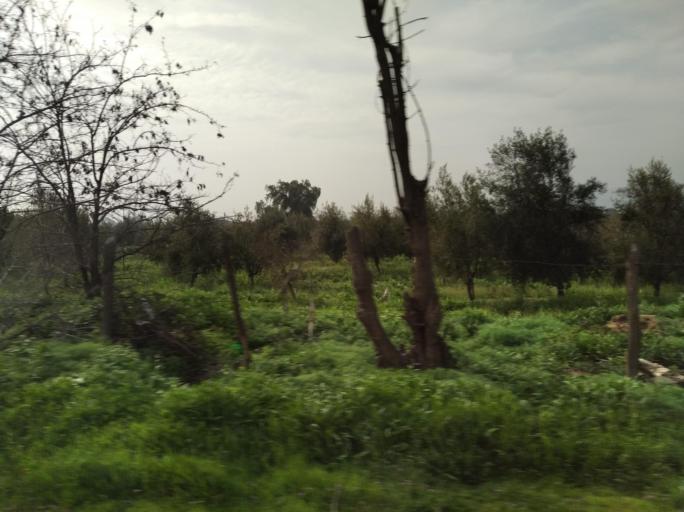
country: CL
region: Santiago Metropolitan
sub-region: Provincia de Chacabuco
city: Lampa
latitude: -33.1655
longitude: -70.8941
